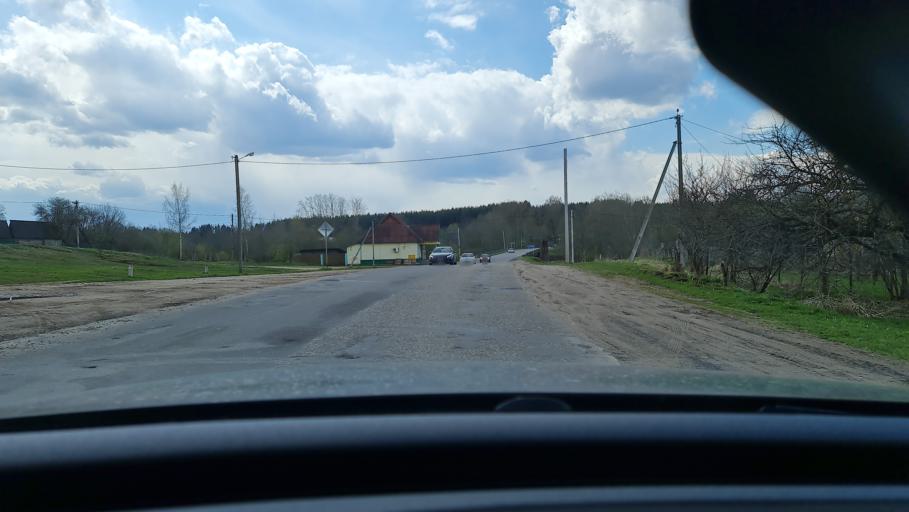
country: RU
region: Tverskaya
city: Toropets
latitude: 56.4243
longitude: 31.6438
